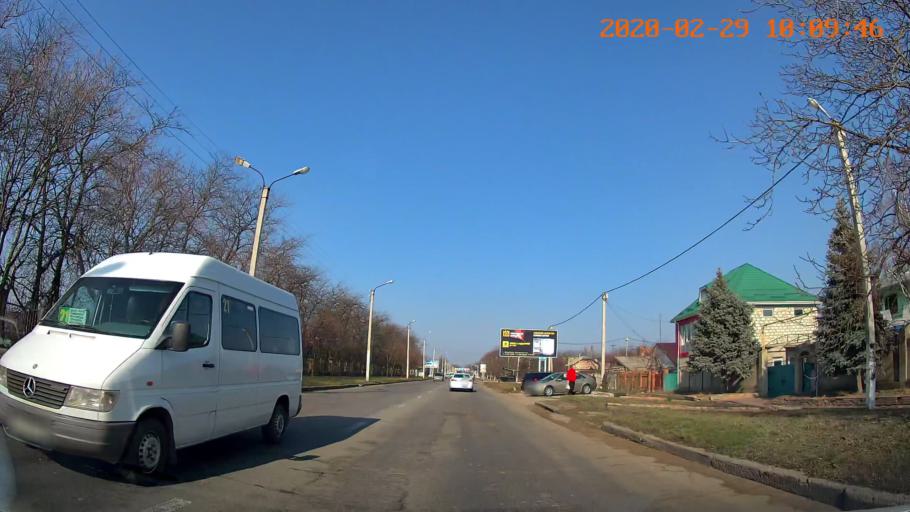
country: MD
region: Telenesti
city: Tiraspolul Nou
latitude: 46.8297
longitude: 29.6497
